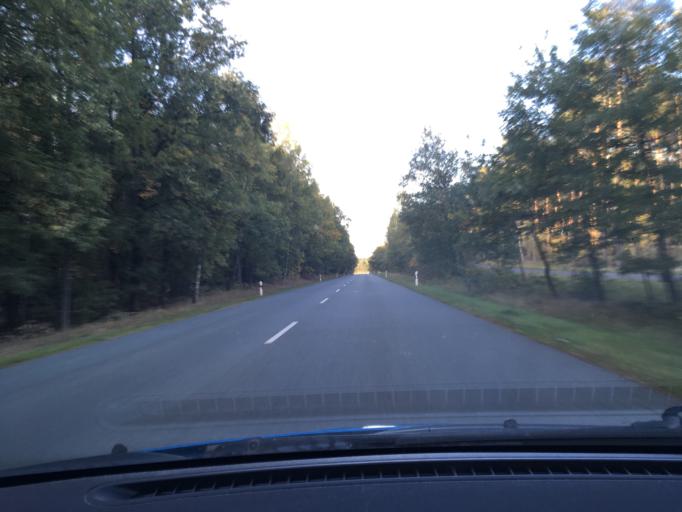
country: DE
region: Lower Saxony
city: Munster
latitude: 53.0237
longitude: 10.0550
